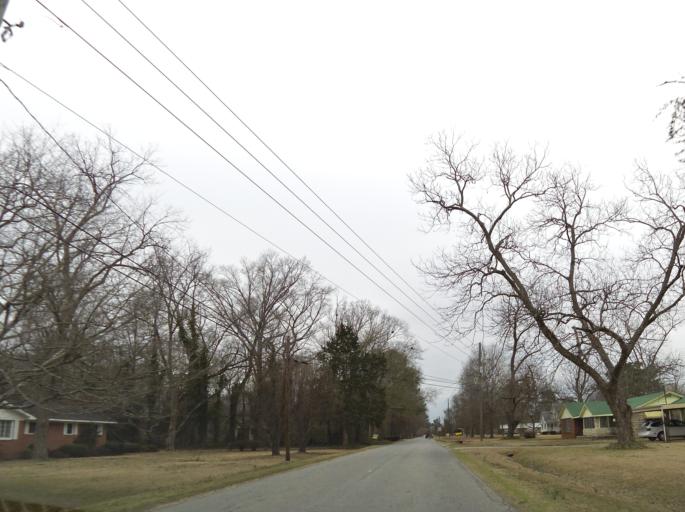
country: US
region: Georgia
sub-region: Houston County
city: Centerville
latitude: 32.7041
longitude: -83.6886
